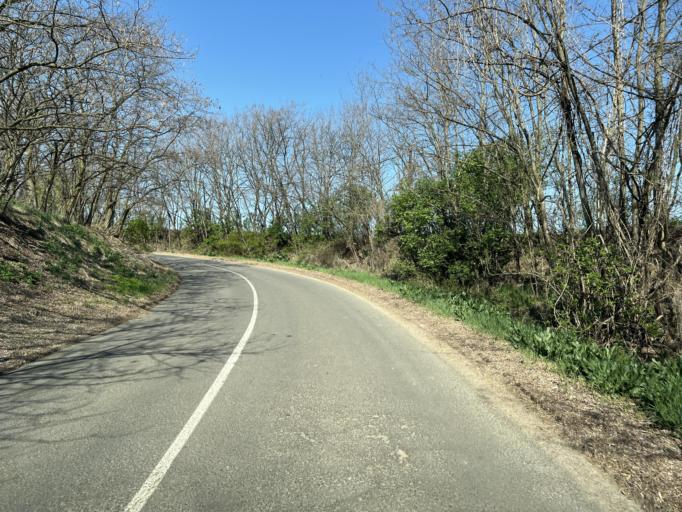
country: HU
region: Pest
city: Orbottyan
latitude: 47.7400
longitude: 19.3043
